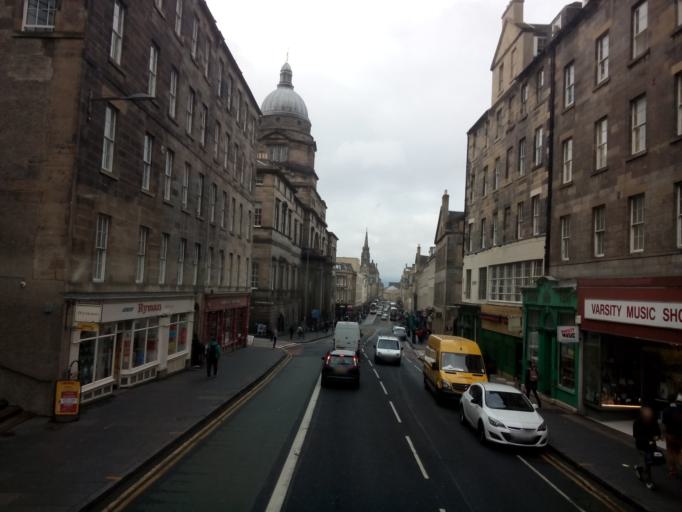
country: GB
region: Scotland
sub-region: Edinburgh
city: Edinburgh
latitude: 55.9467
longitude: -3.1857
